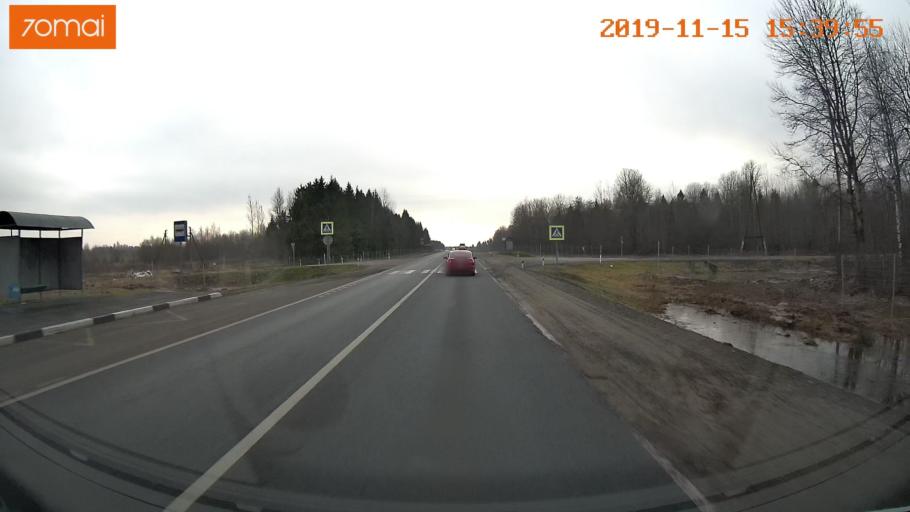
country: RU
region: Jaroslavl
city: Danilov
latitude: 58.0170
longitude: 40.0624
